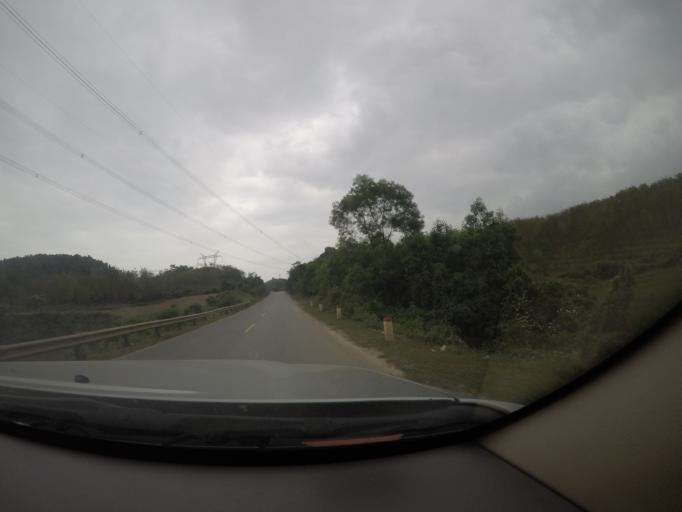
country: VN
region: Quang Binh
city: Hoan Lao
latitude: 17.6027
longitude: 106.4126
